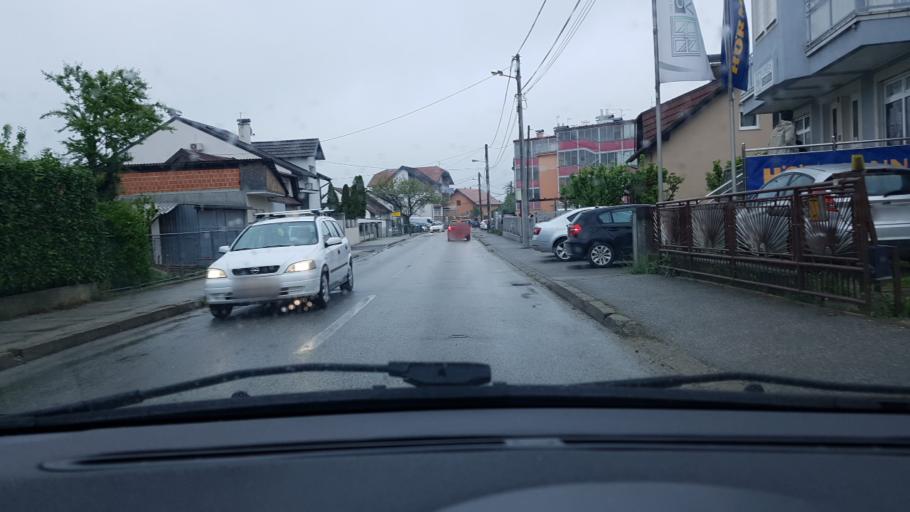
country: HR
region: Grad Zagreb
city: Dubrava
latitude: 45.8167
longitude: 16.0575
